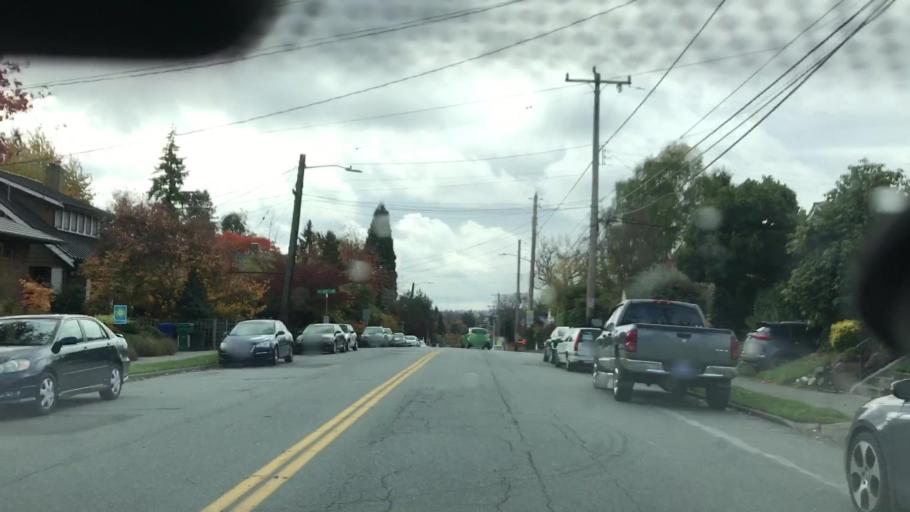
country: US
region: Washington
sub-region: King County
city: Seattle
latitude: 47.6791
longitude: -122.3120
